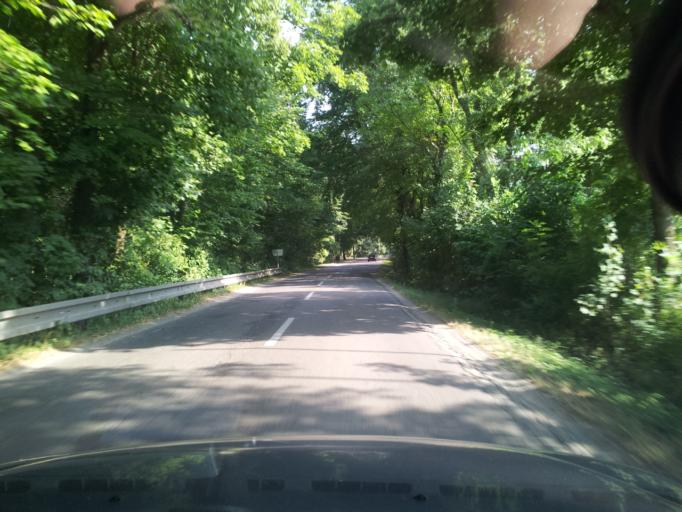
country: SK
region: Nitriansky
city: Trencianske Teplice
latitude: 48.8336
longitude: 18.1855
